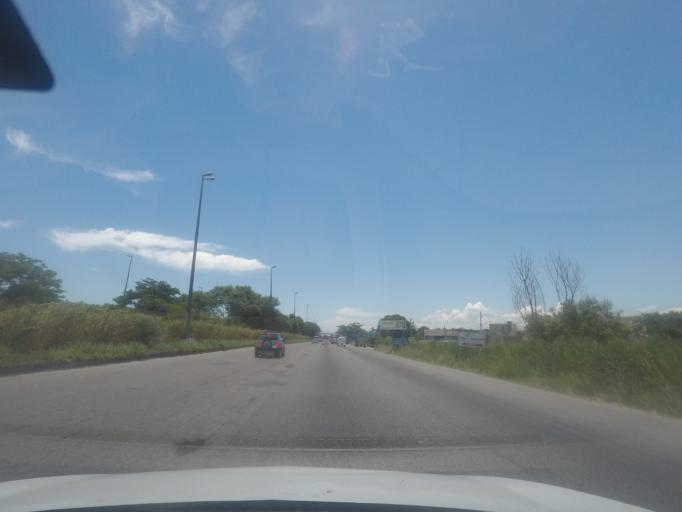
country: BR
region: Rio de Janeiro
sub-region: Itaguai
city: Itaguai
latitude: -22.8906
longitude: -43.6661
